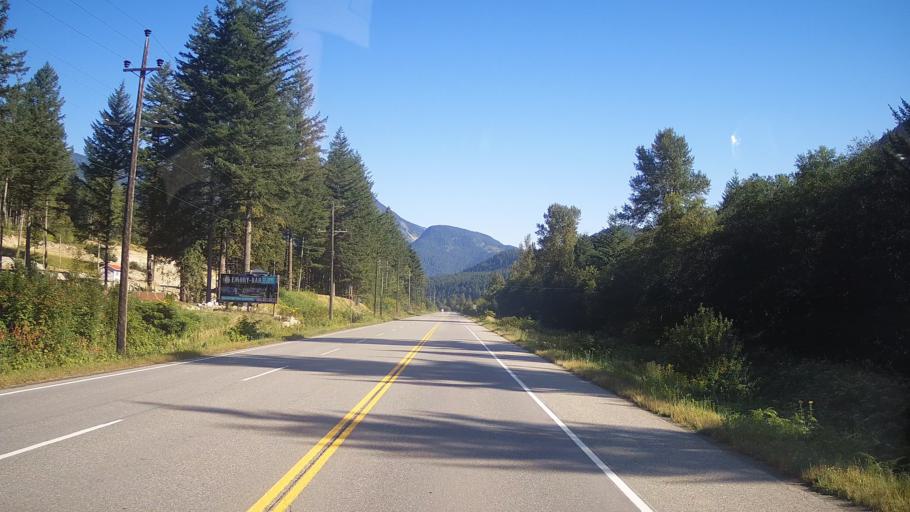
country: CA
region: British Columbia
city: Hope
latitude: 49.5207
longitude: -121.4209
